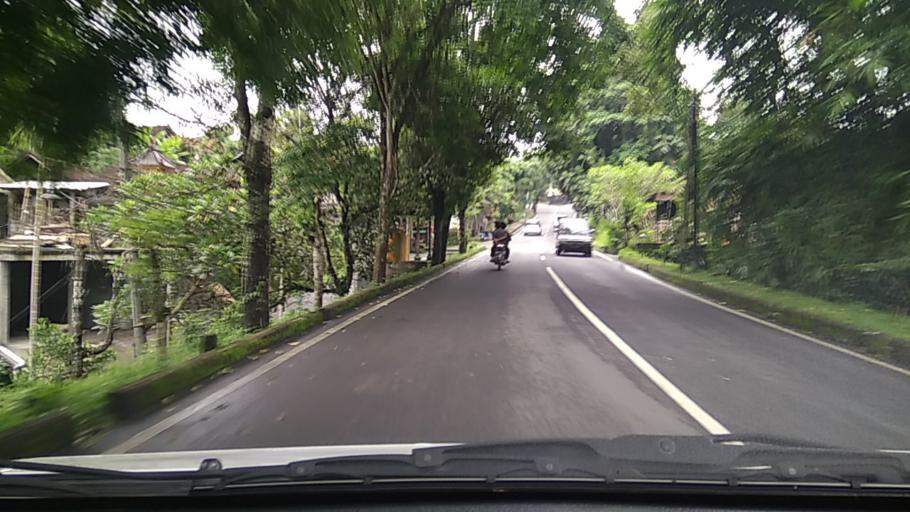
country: ID
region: Bali
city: Banjar Manukayaanyar
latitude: -8.4193
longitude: 115.3107
